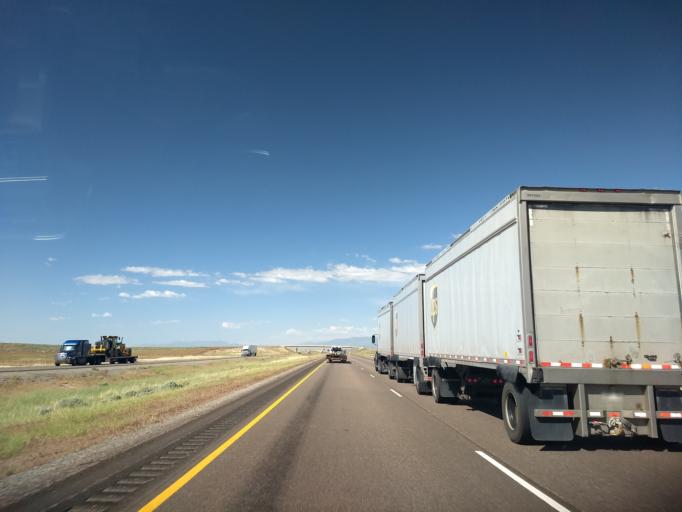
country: US
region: Utah
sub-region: Millard County
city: Fillmore
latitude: 38.7412
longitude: -112.5810
